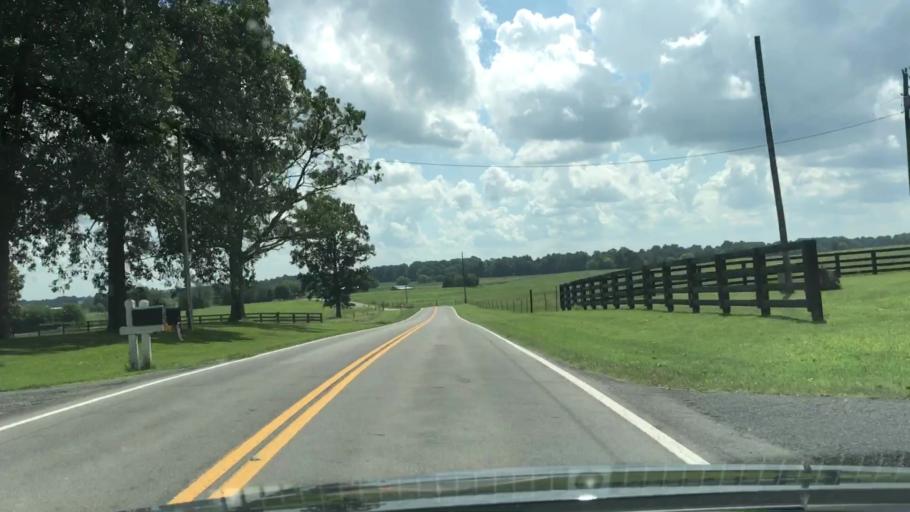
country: US
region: Tennessee
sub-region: Robertson County
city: Springfield
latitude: 36.5903
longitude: -86.8970
